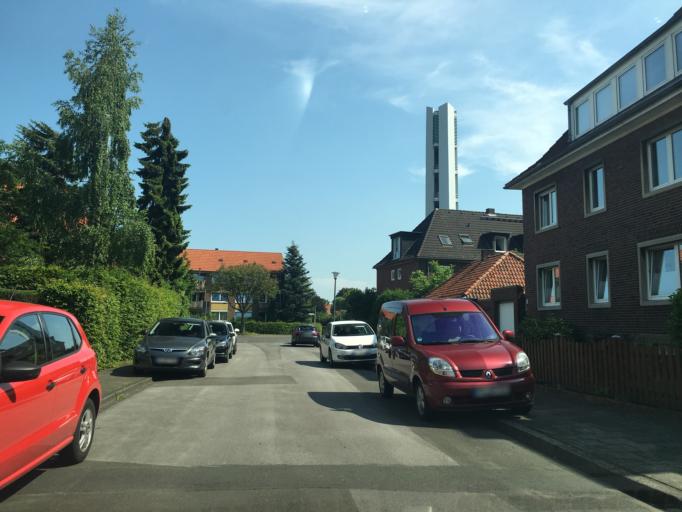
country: DE
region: North Rhine-Westphalia
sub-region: Regierungsbezirk Munster
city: Muenster
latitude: 51.9700
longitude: 7.6502
